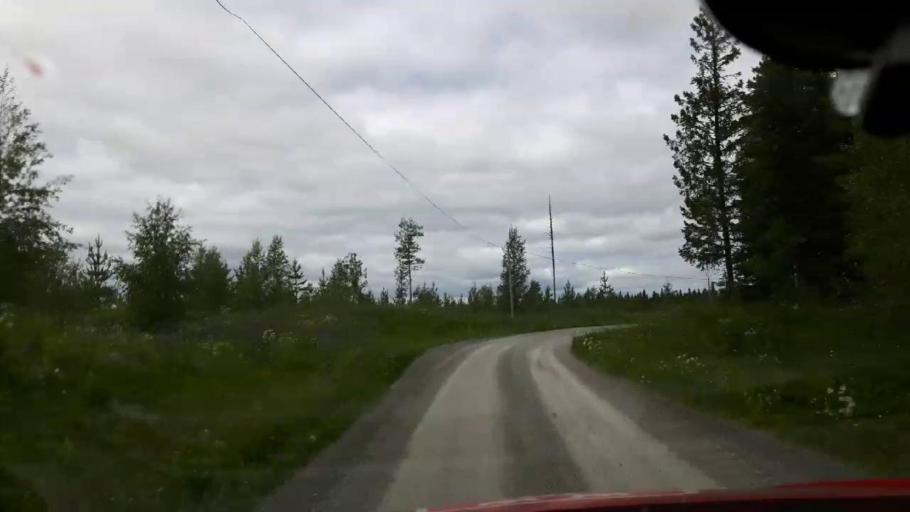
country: SE
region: Jaemtland
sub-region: OEstersunds Kommun
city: Brunflo
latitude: 63.0566
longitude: 14.9125
